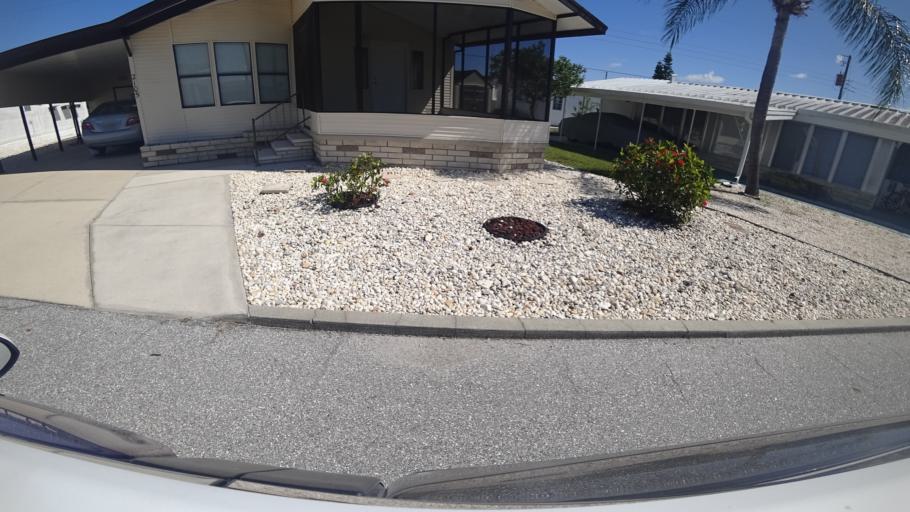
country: US
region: Florida
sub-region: Manatee County
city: Bayshore Gardens
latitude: 27.4210
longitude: -82.5827
